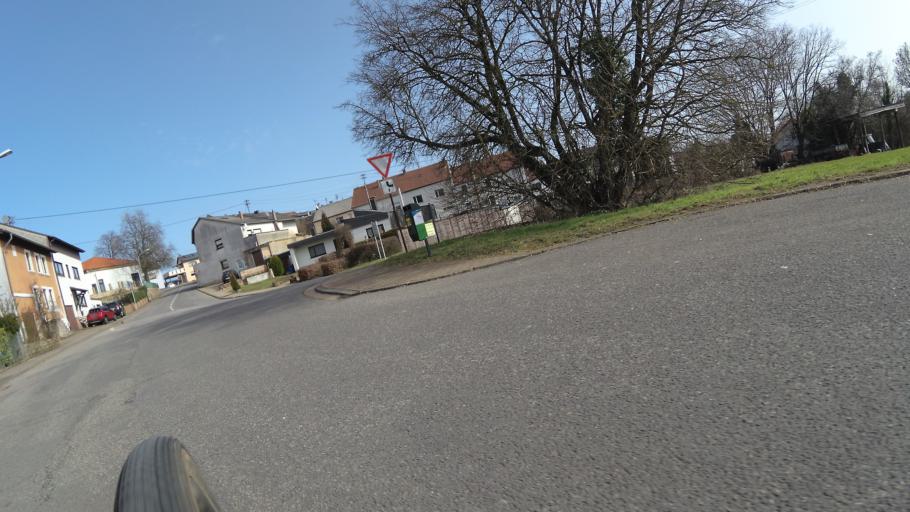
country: DE
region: Saarland
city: Uberherrn
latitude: 49.2635
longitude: 6.6939
